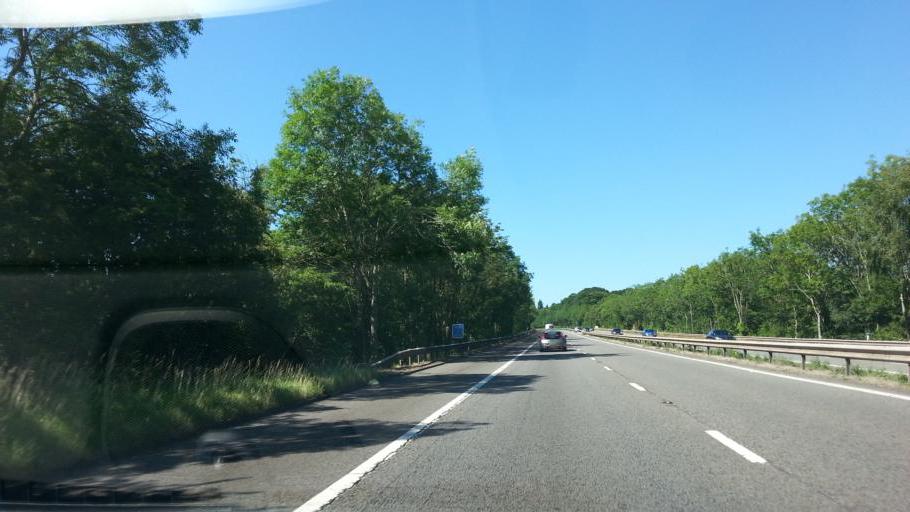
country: GB
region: England
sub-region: Gloucestershire
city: Newent
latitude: 51.9582
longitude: -2.4395
